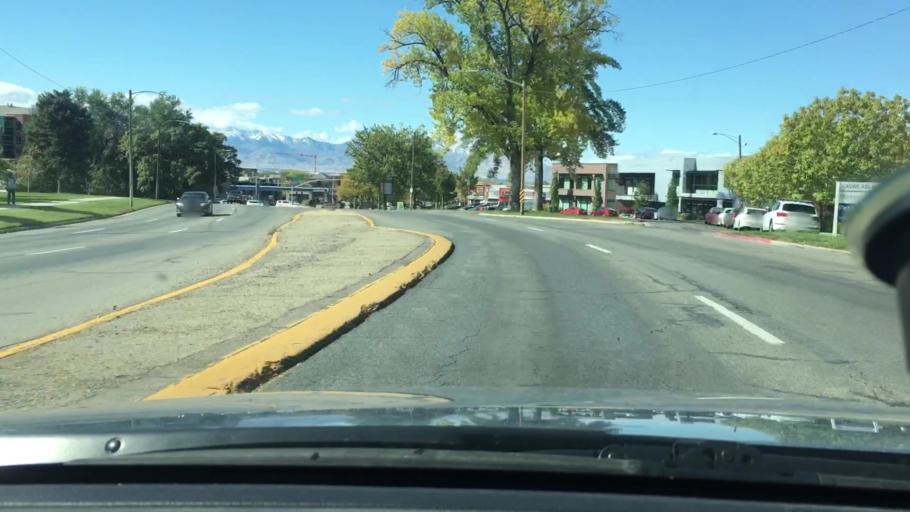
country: US
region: Utah
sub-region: Salt Lake County
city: Willard
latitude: 40.7259
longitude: -111.8514
